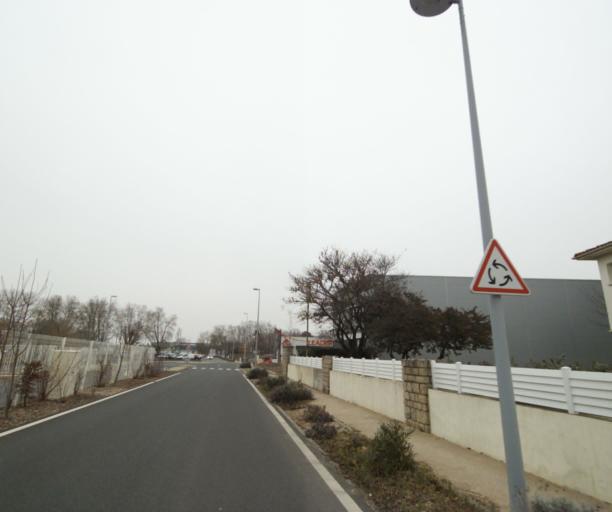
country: FR
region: Poitou-Charentes
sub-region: Departement des Deux-Sevres
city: Bessines
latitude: 46.3059
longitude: -0.4848
